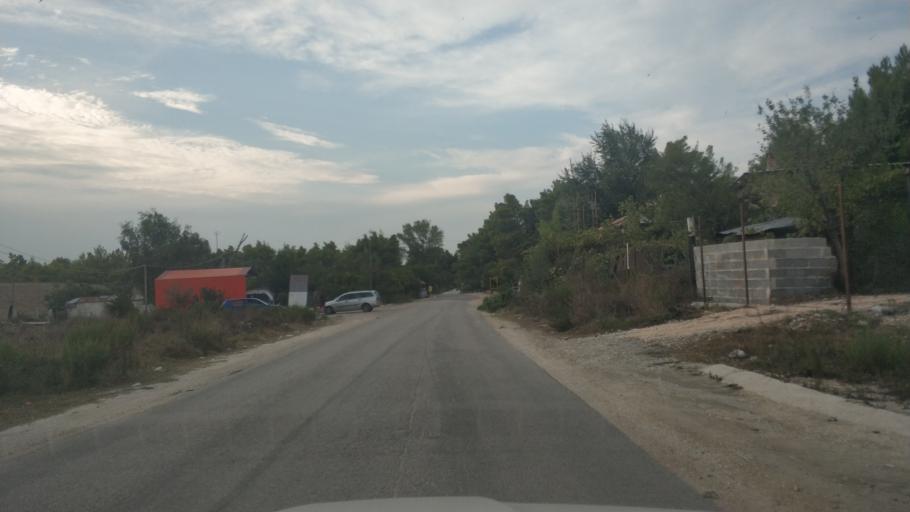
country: AL
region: Vlore
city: Vlore
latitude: 40.4773
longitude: 19.4526
